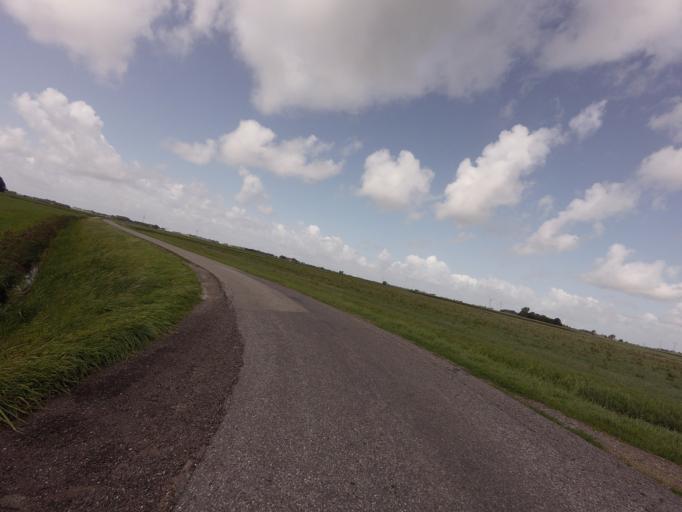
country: NL
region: Friesland
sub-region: Gemeente Franekeradeel
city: Sexbierum
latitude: 53.1651
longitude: 5.4868
